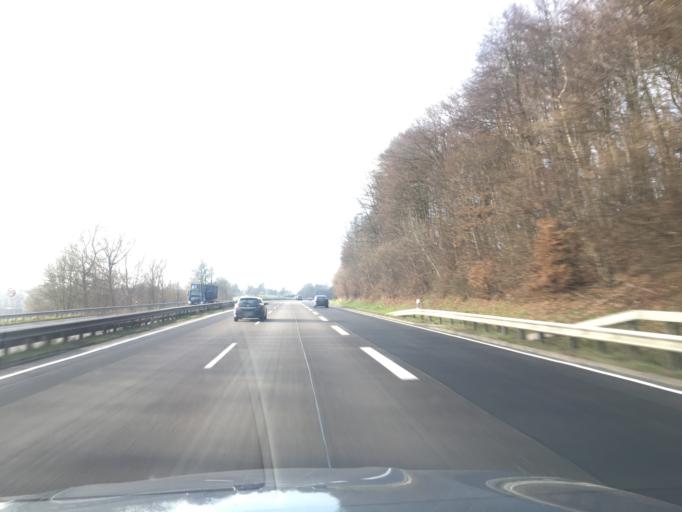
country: DE
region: Rheinland-Pfalz
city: Hohr-Grenzhausen
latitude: 50.4459
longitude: 7.6702
